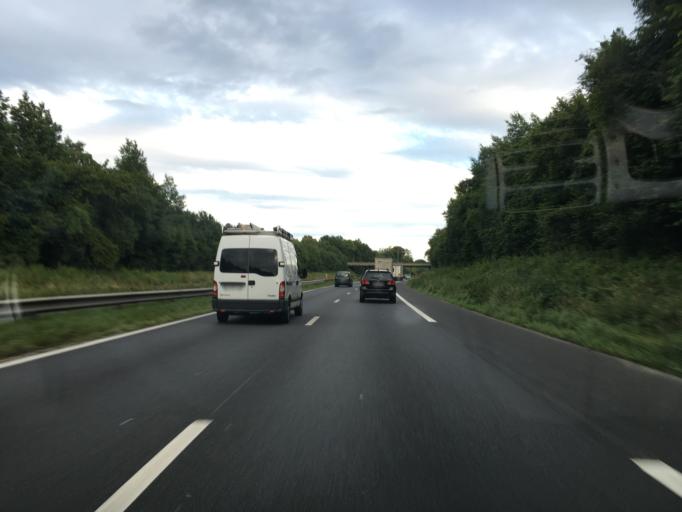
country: FR
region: Ile-de-France
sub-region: Departement de Seine-et-Marne
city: Brie-Comte-Robert
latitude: 48.6801
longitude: 2.6061
